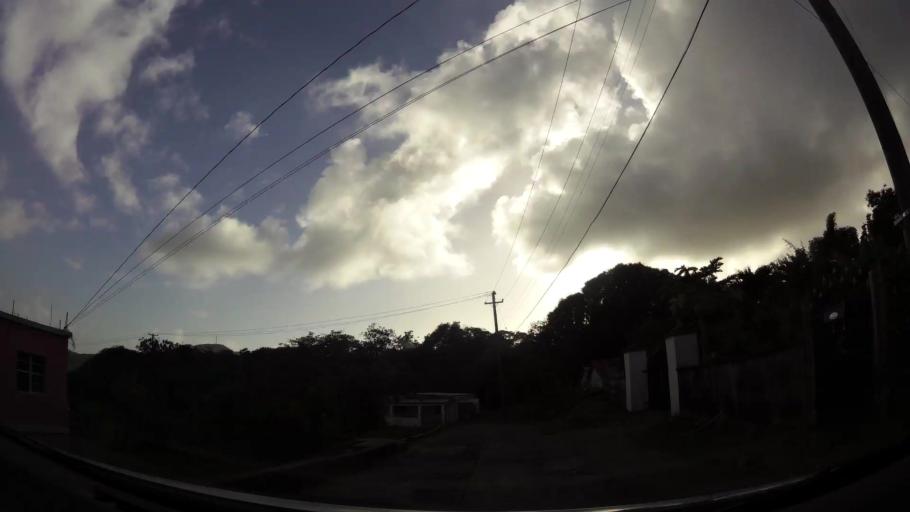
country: KN
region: Saint George Gingerland
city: Market Shop
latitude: 17.1342
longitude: -62.5734
